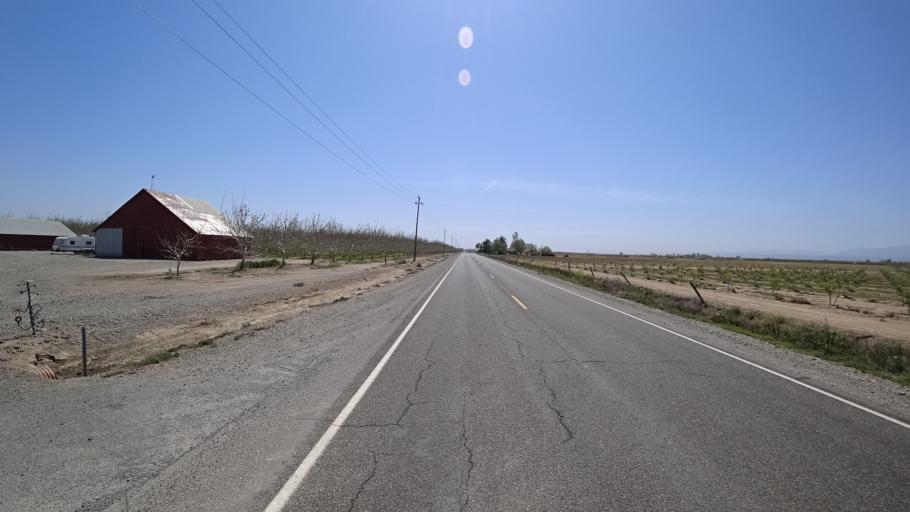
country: US
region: California
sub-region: Glenn County
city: Orland
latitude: 39.6594
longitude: -122.1971
